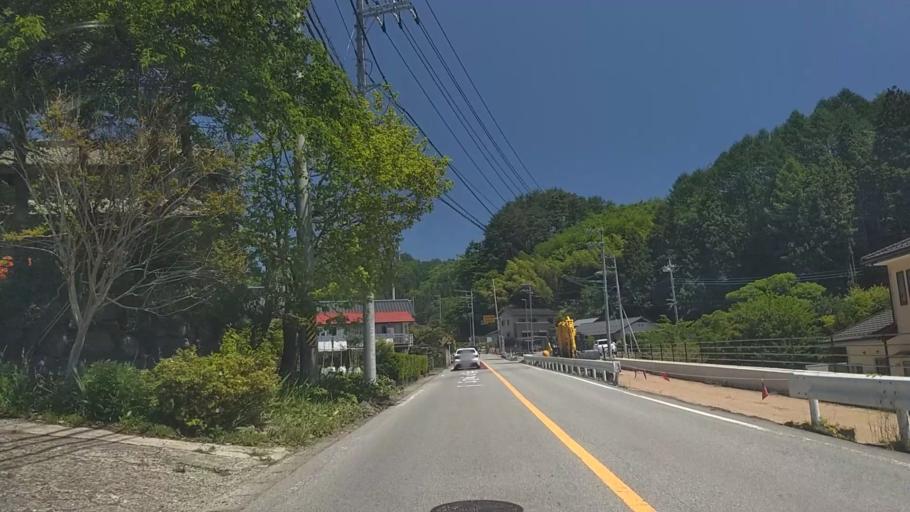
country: JP
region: Yamanashi
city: Nirasaki
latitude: 35.8713
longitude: 138.4280
